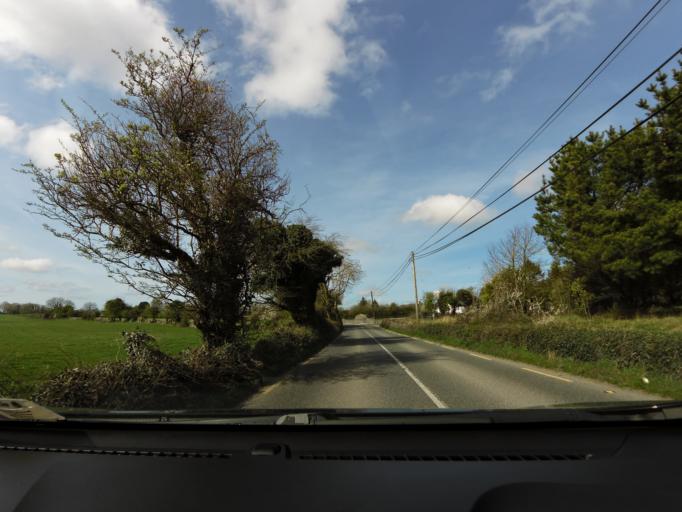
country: IE
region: Connaught
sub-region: County Galway
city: Athenry
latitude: 53.3060
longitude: -8.7727
